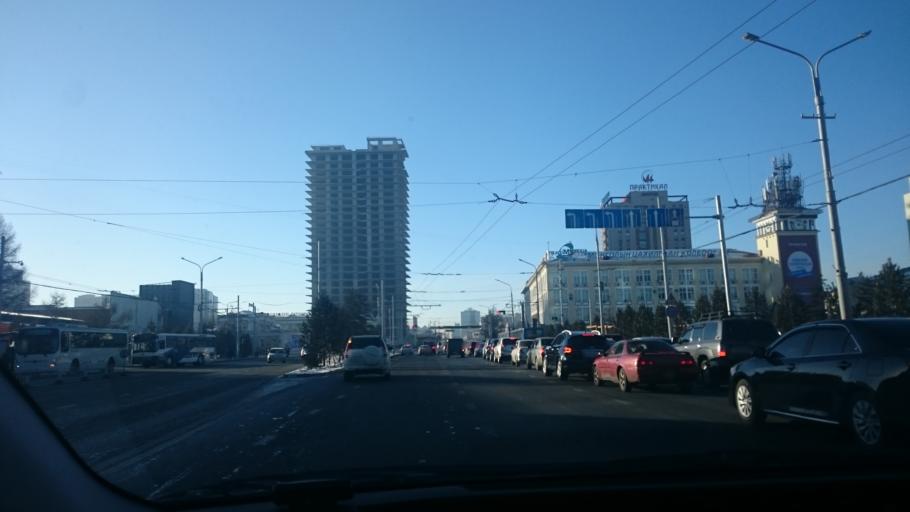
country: MN
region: Ulaanbaatar
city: Ulaanbaatar
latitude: 47.9170
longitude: 106.9183
